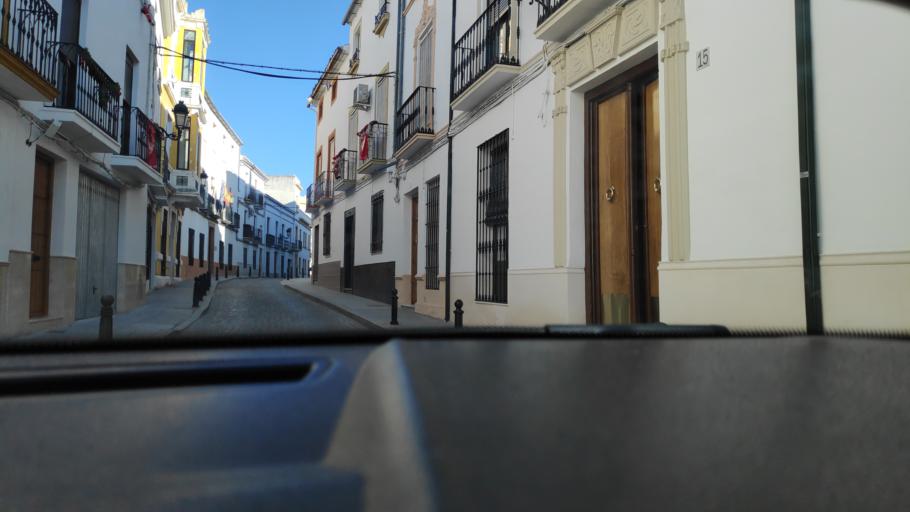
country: ES
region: Andalusia
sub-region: Province of Cordoba
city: Baena
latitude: 37.6146
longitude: -4.3276
